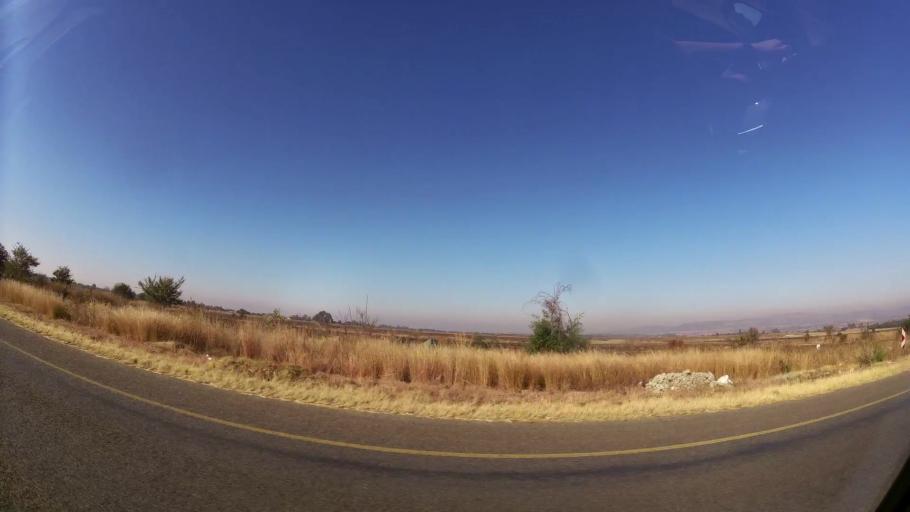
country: ZA
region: Gauteng
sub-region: City of Johannesburg Metropolitan Municipality
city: Johannesburg
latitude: -26.3129
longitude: 28.0771
